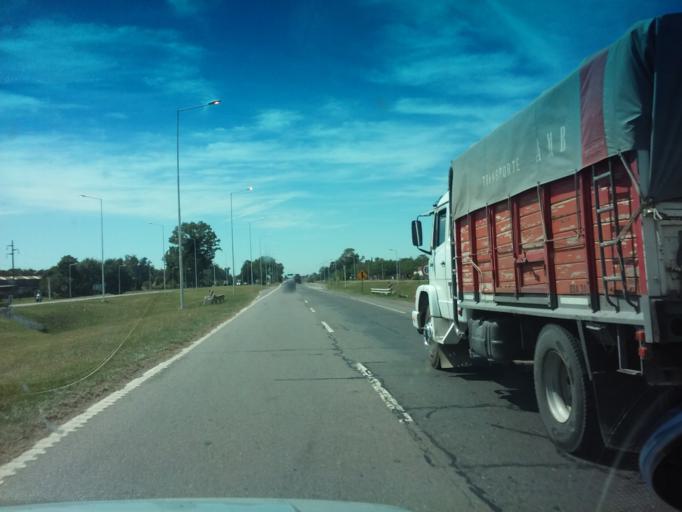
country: AR
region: Buenos Aires
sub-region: Partido de Mercedes
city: Mercedes
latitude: -34.6647
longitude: -59.3990
